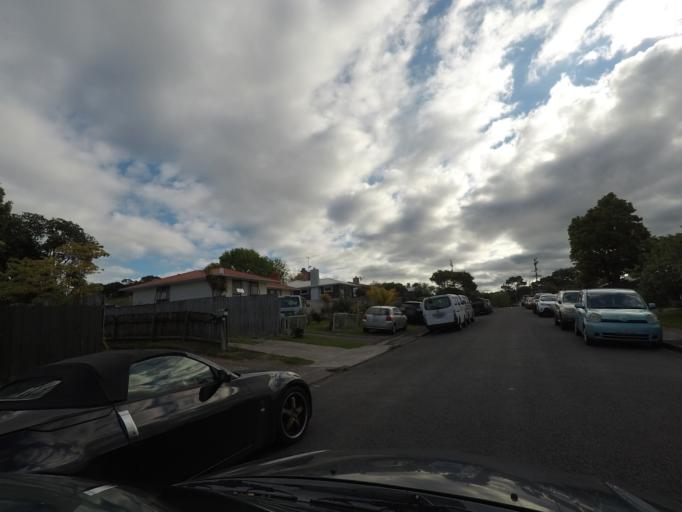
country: NZ
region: Auckland
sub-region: Auckland
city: Rosebank
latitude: -36.8820
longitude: 174.6576
